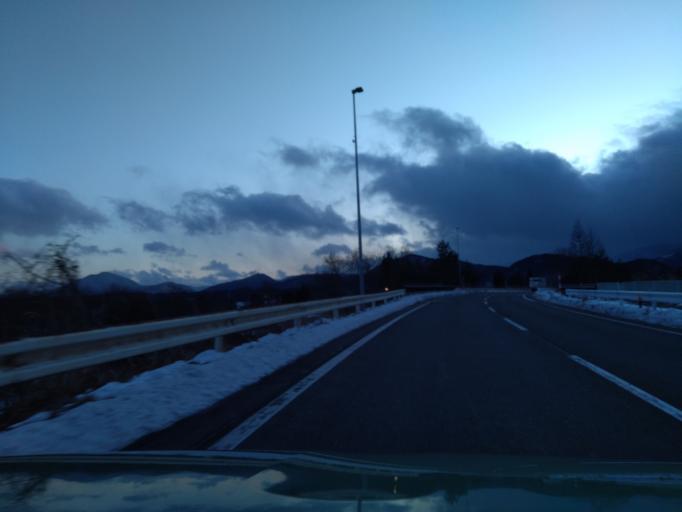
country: JP
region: Iwate
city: Shizukuishi
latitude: 39.6937
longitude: 140.9353
